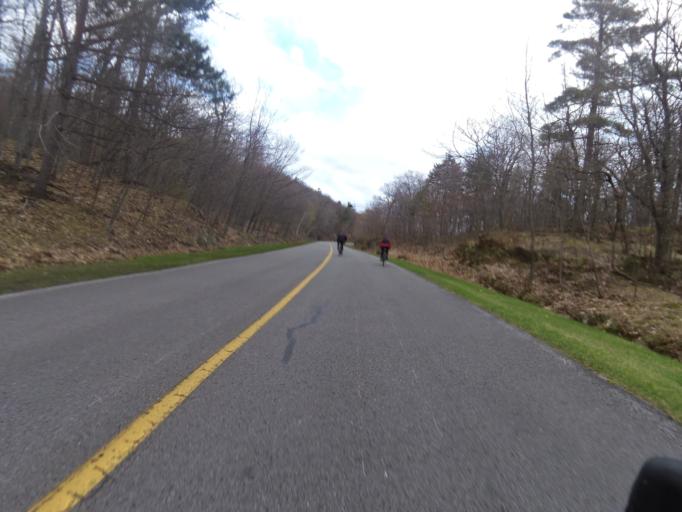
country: CA
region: Quebec
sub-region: Outaouais
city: Gatineau
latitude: 45.4922
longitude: -75.8667
